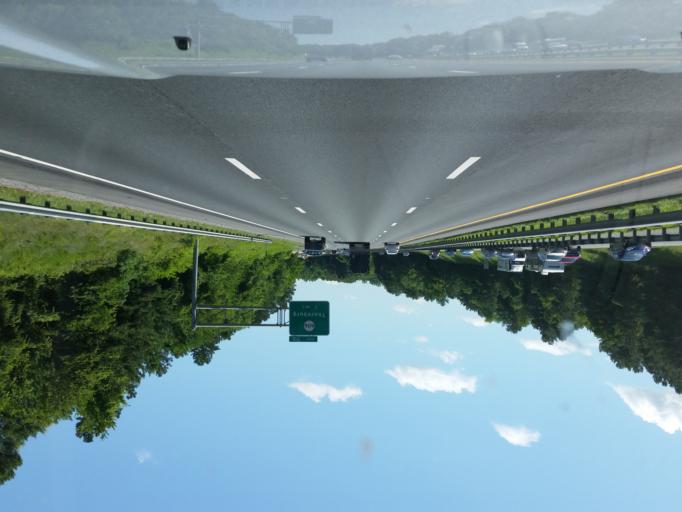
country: US
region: Virginia
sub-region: Spotsylvania County
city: Spotsylvania Courthouse
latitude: 38.1510
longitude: -77.5063
